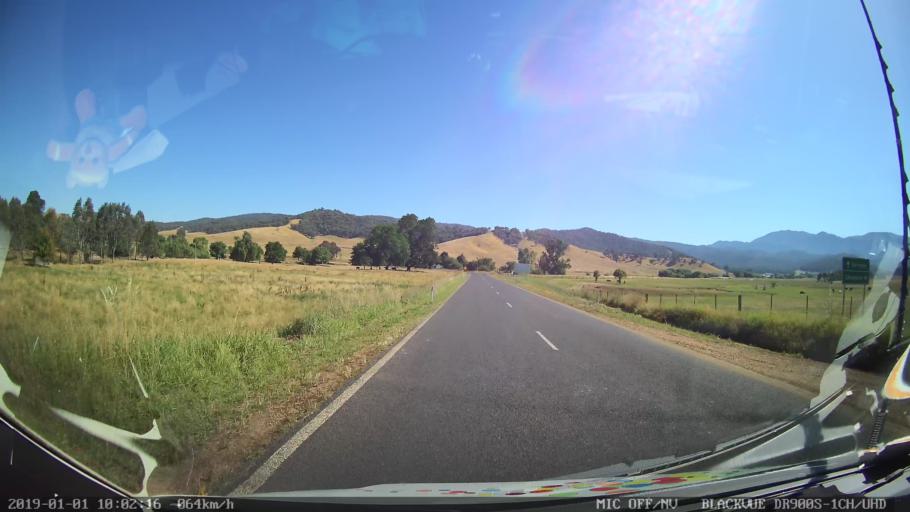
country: AU
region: New South Wales
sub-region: Snowy River
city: Jindabyne
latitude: -36.1830
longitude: 148.1018
